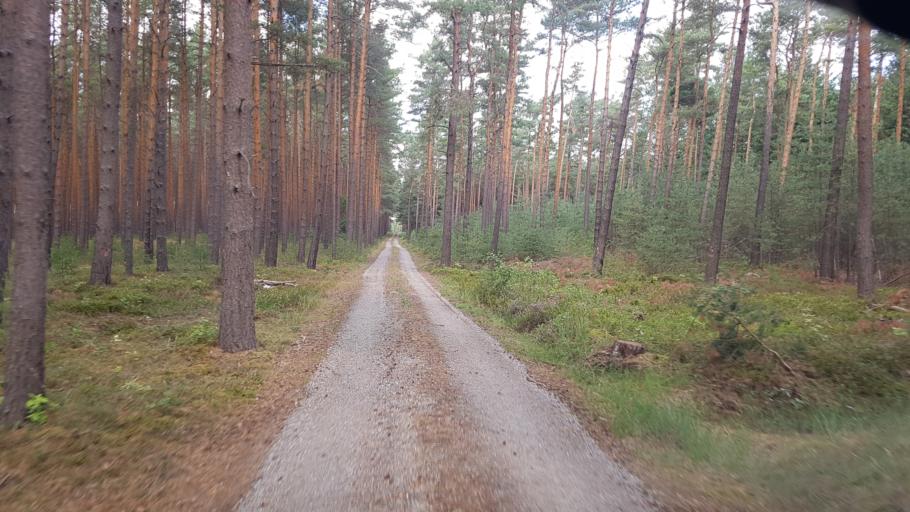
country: DE
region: Brandenburg
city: Crinitz
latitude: 51.7067
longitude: 13.7676
